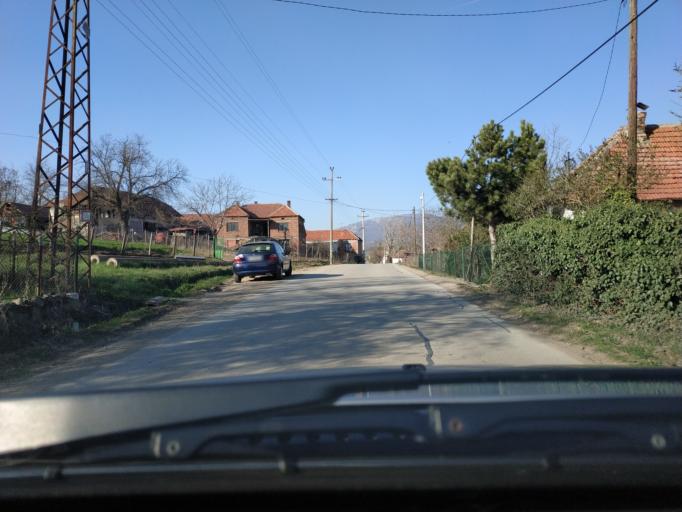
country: RS
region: Central Serbia
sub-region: Nisavski Okrug
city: Aleksinac
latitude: 43.5071
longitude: 21.7963
